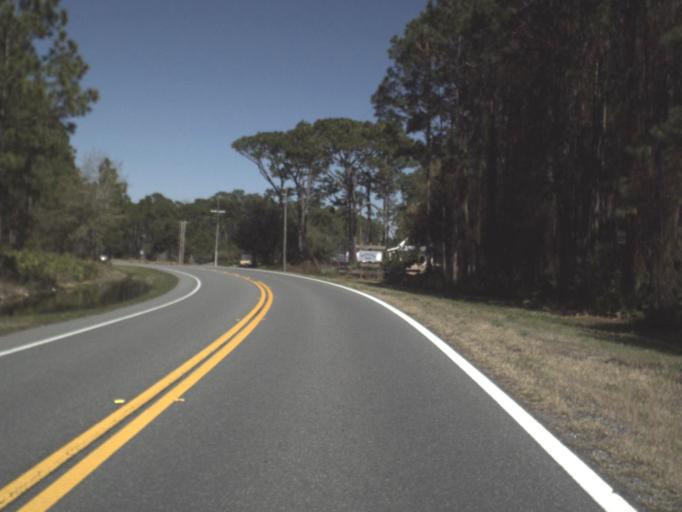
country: US
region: Florida
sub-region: Franklin County
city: Carrabelle
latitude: 29.9141
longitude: -84.5261
